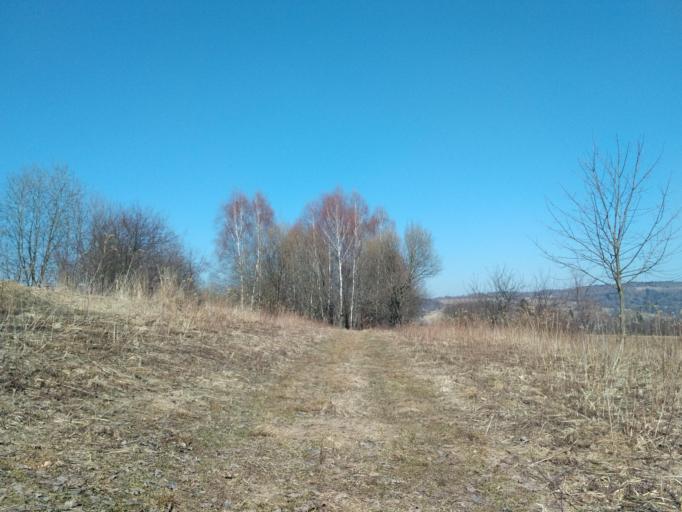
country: PL
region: Subcarpathian Voivodeship
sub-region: Powiat brzozowski
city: Golcowa
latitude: 49.7610
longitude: 22.0315
